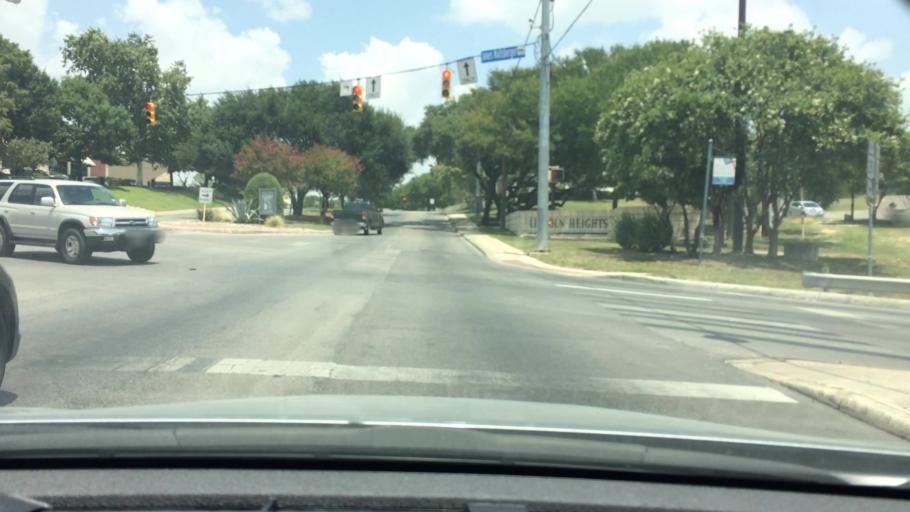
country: US
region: Texas
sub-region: Bexar County
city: Olmos Park
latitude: 29.4912
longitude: -98.4820
